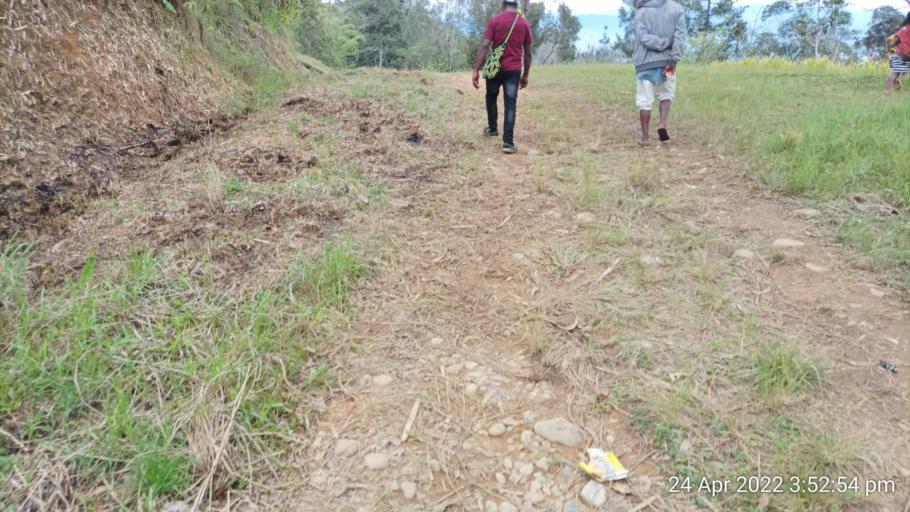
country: PG
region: Jiwaka
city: Minj
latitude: -5.8978
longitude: 144.8235
